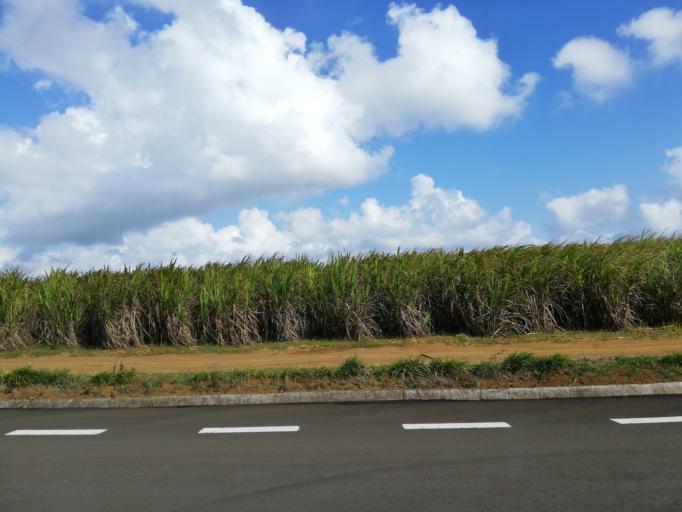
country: MU
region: Moka
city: Verdun
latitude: -20.2241
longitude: 57.5598
